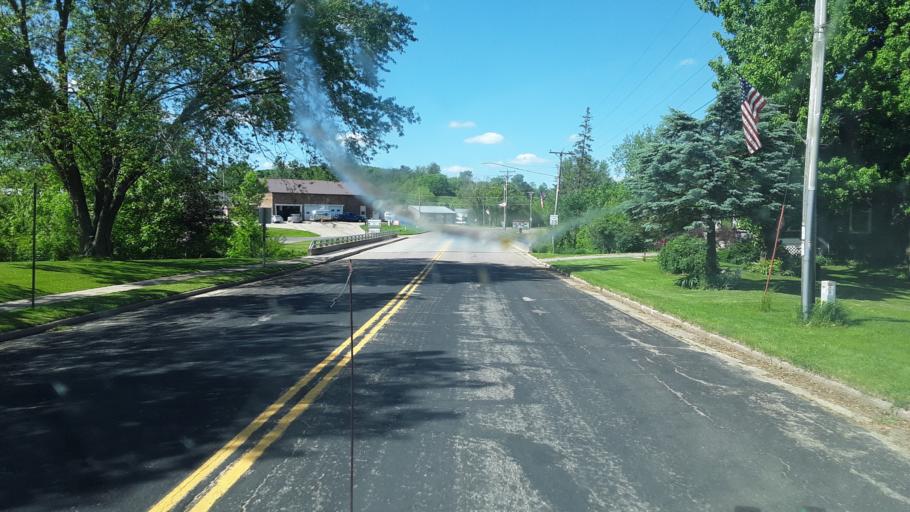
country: US
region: Wisconsin
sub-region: Sauk County
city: Reedsburg
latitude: 43.5246
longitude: -90.1961
